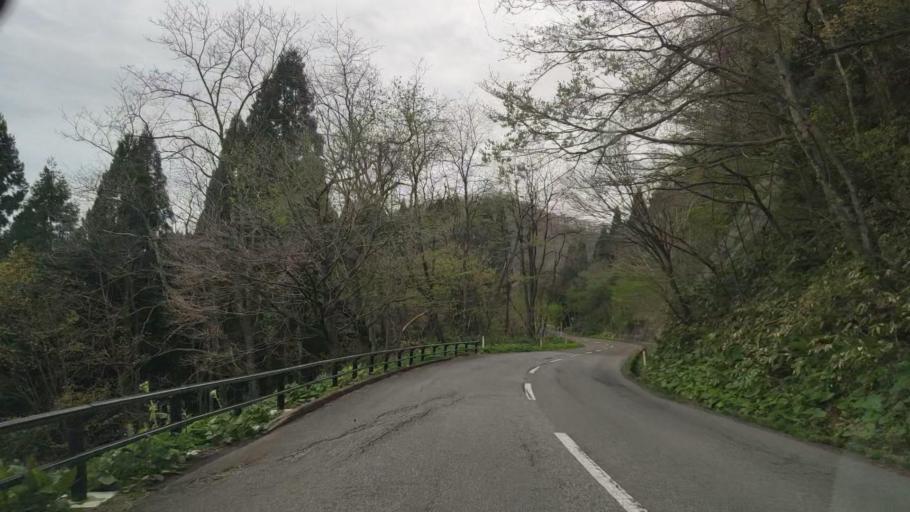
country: JP
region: Akita
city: Hanawa
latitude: 40.3726
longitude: 140.7888
